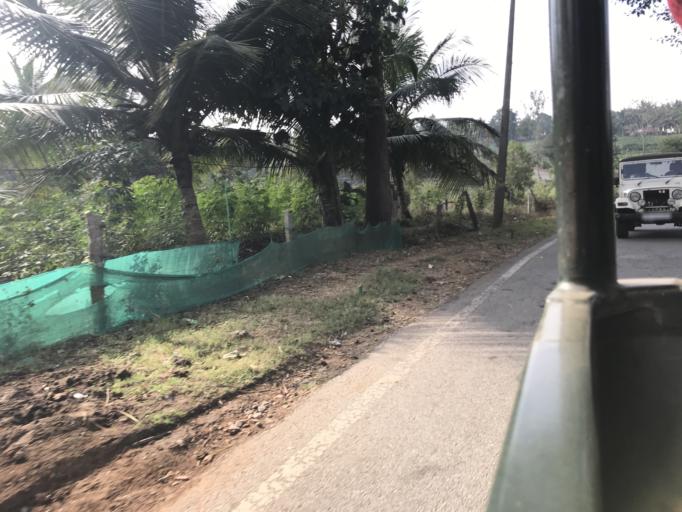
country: IN
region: Karnataka
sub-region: Mysore
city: Heggadadevankote
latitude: 11.9467
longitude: 76.2469
